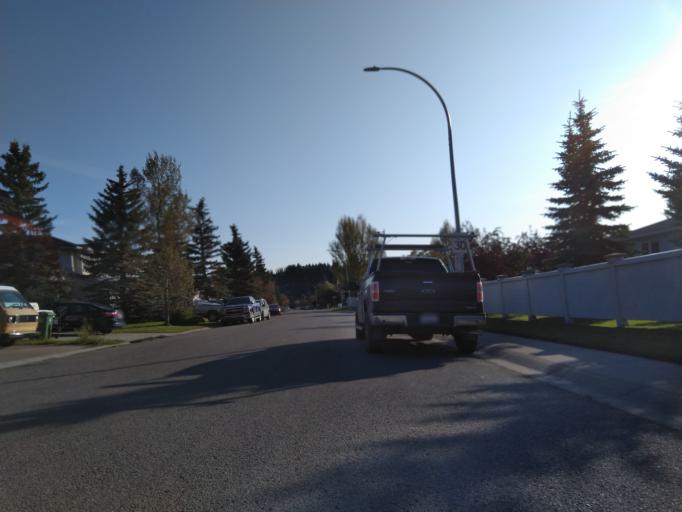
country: CA
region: Alberta
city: Cochrane
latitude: 51.1787
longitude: -114.4756
